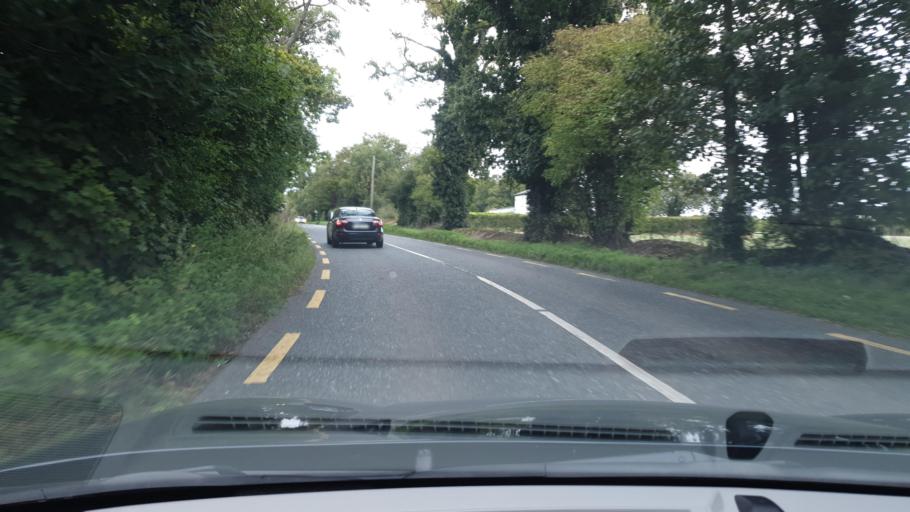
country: IE
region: Leinster
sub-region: Kildare
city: Clane
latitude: 53.2732
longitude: -6.6880
